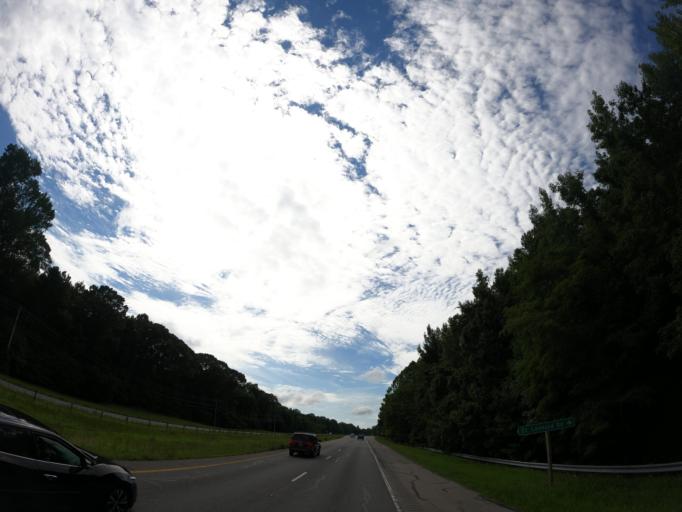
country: US
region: Maryland
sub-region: Calvert County
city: Long Beach
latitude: 38.4472
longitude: -76.4834
